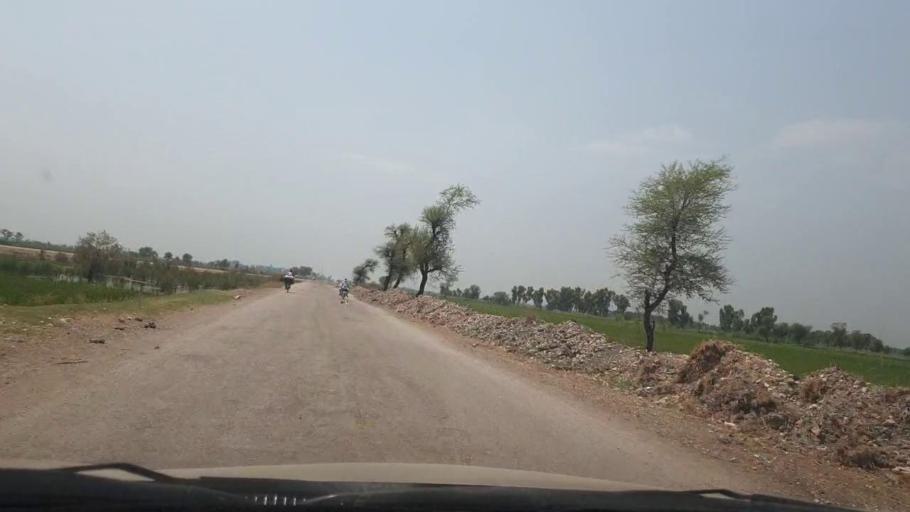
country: PK
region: Sindh
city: Ratodero
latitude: 27.7162
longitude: 68.2775
